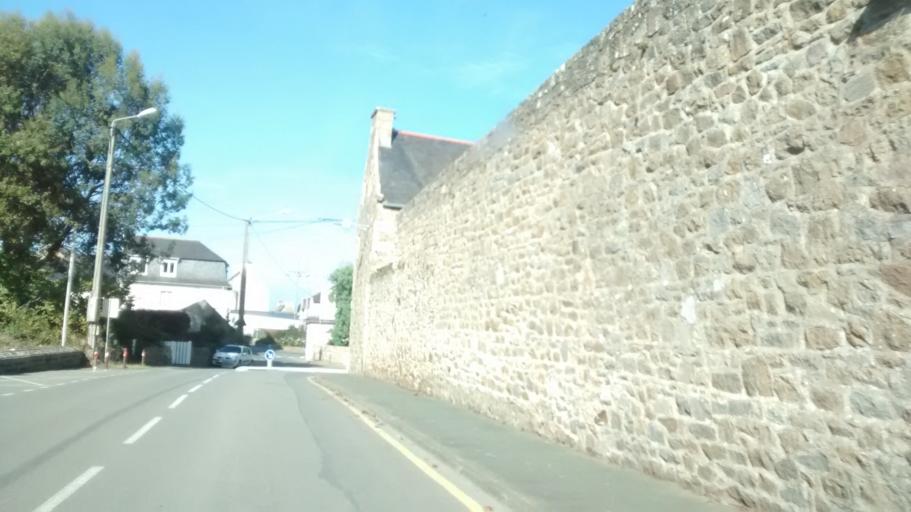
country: FR
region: Brittany
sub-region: Departement des Cotes-d'Armor
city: Trebeurden
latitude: 48.7680
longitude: -3.5633
